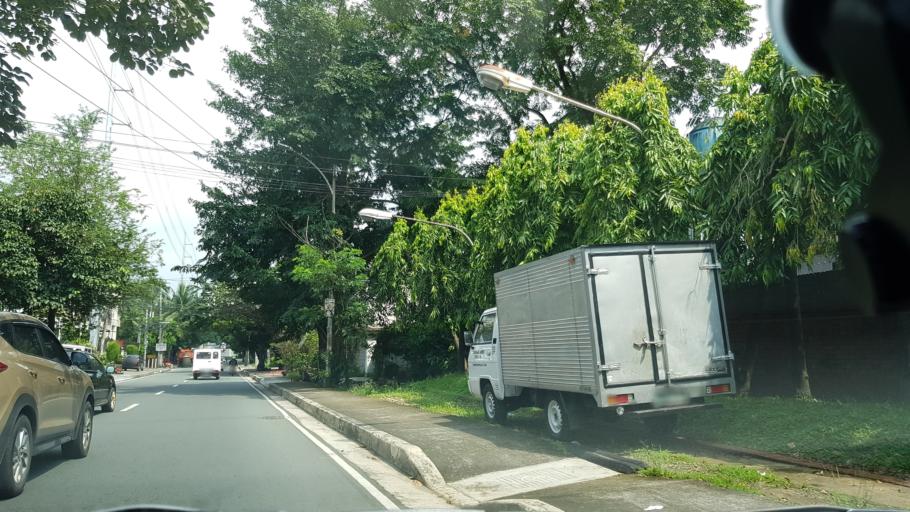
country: PH
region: Metro Manila
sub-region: San Juan
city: San Juan
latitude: 14.6188
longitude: 121.0347
